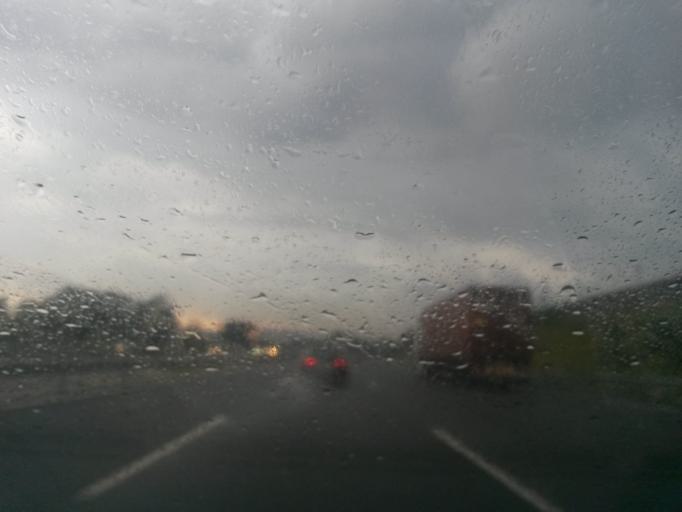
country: ES
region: Catalonia
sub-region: Provincia de Girona
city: Salt
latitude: 41.9928
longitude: 2.7921
